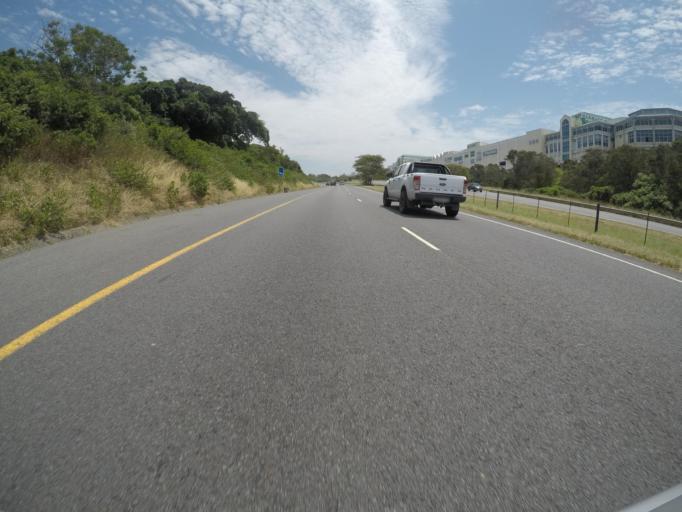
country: ZA
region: Eastern Cape
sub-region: Buffalo City Metropolitan Municipality
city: East London
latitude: -32.9726
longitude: 27.9016
